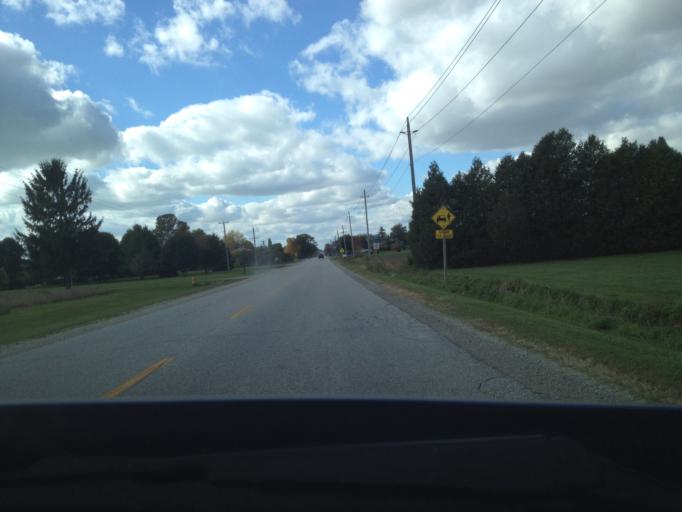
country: CA
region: Ontario
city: Amherstburg
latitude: 42.0322
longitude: -82.5570
